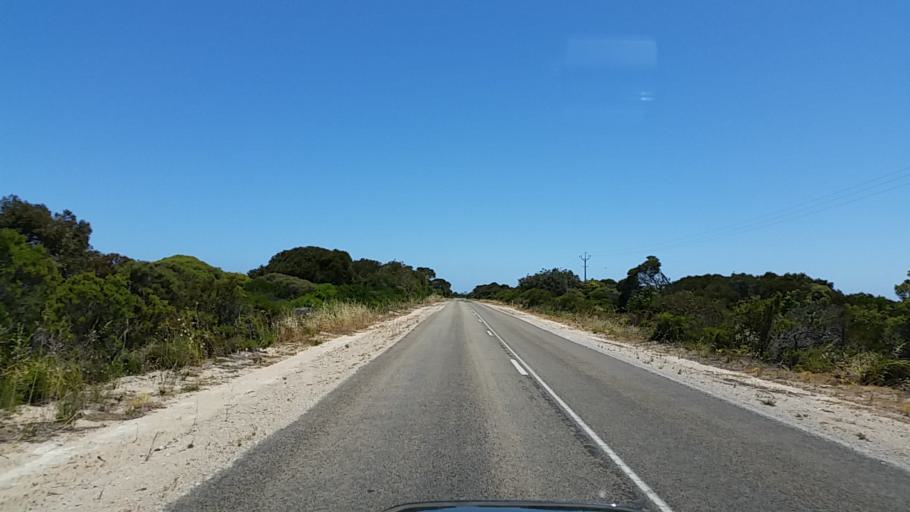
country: AU
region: South Australia
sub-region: Yorke Peninsula
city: Honiton
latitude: -35.2180
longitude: 137.0006
